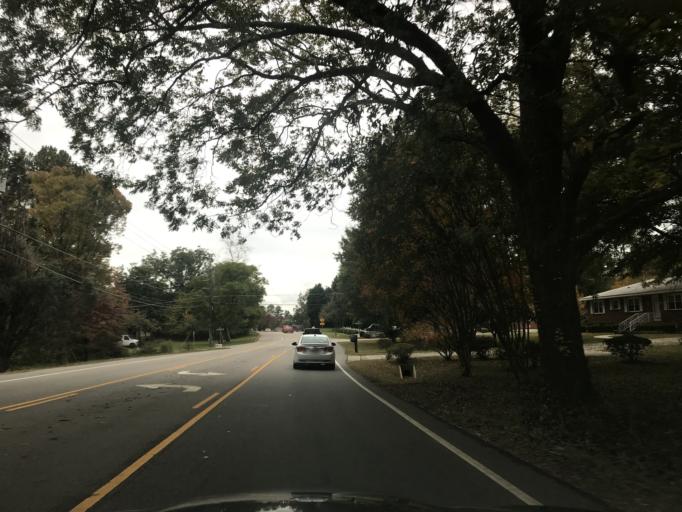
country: US
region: North Carolina
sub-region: Wake County
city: Raleigh
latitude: 35.8658
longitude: -78.5981
